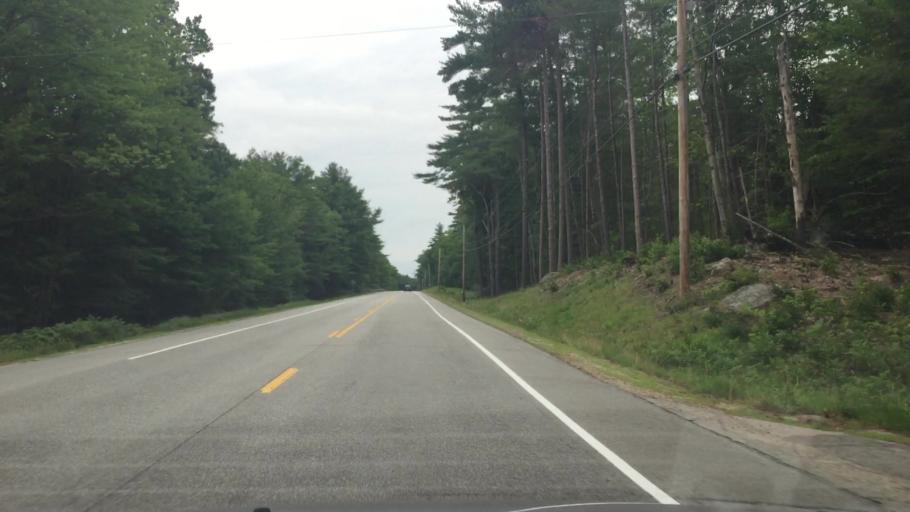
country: US
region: New Hampshire
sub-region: Carroll County
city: Sandwich
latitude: 43.7905
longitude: -71.3754
